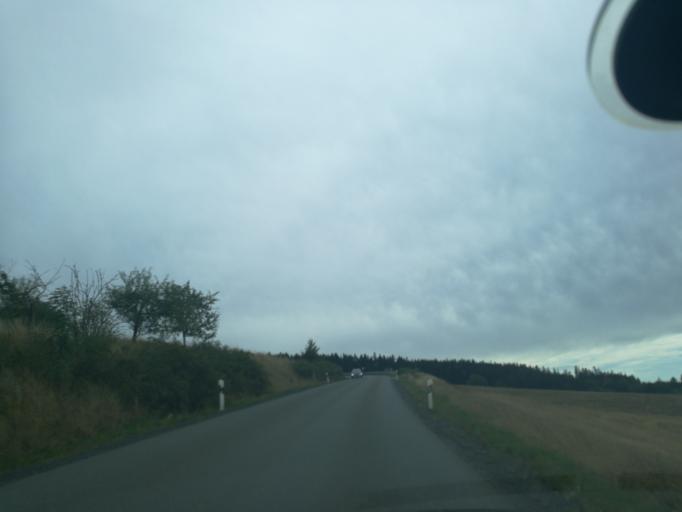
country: DE
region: Bavaria
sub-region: Upper Franconia
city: Dohlau
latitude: 50.2964
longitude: 11.9719
